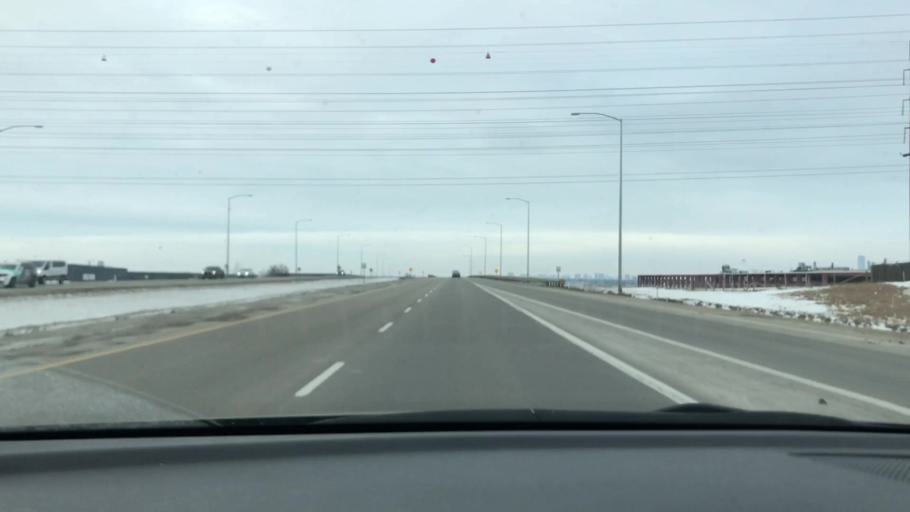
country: CA
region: Alberta
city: Sherwood Park
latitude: 53.5176
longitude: -113.3800
